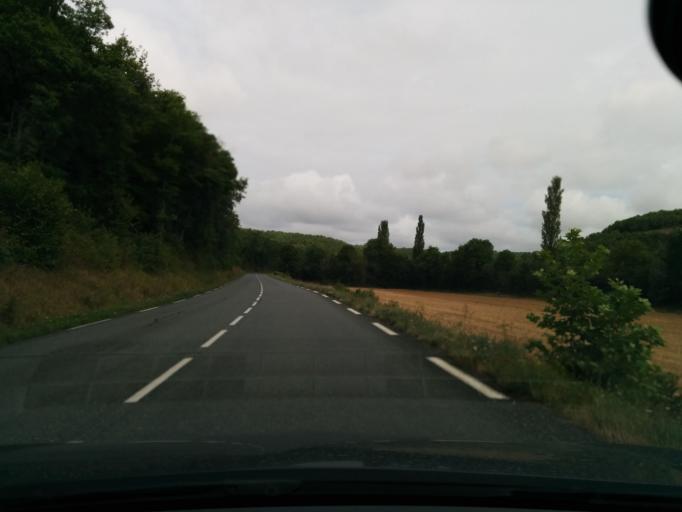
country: FR
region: Midi-Pyrenees
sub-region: Departement du Lot
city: Le Vigan
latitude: 44.6942
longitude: 1.4834
